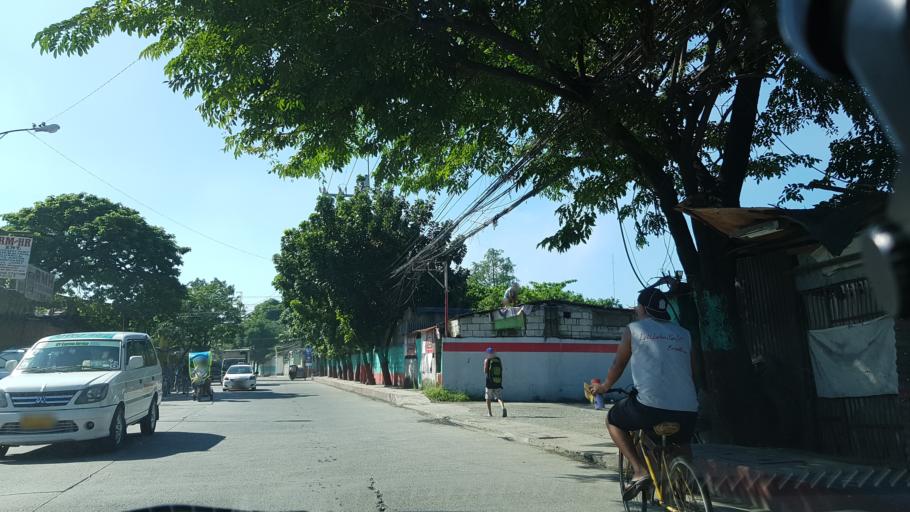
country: PH
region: Calabarzon
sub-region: Province of Rizal
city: Pateros
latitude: 14.5609
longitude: 121.0945
